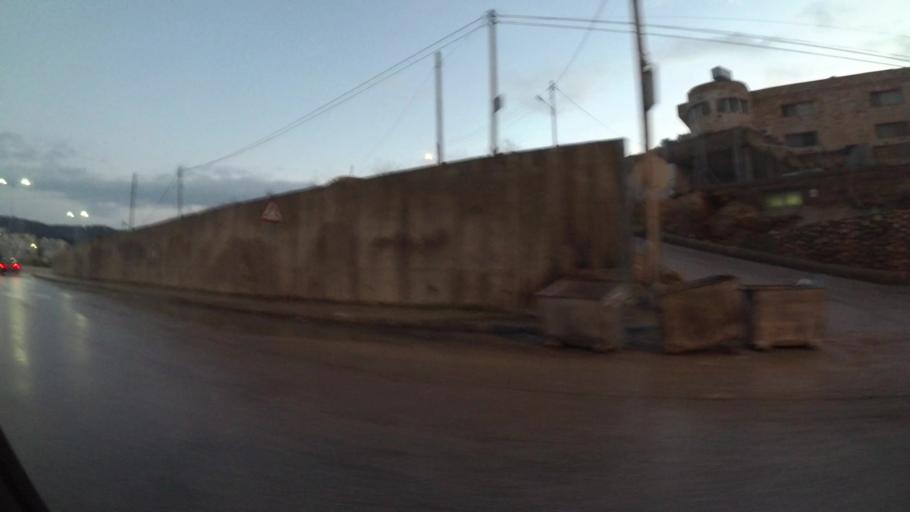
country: JO
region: Amman
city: Al Jubayhah
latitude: 32.0273
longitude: 35.7992
